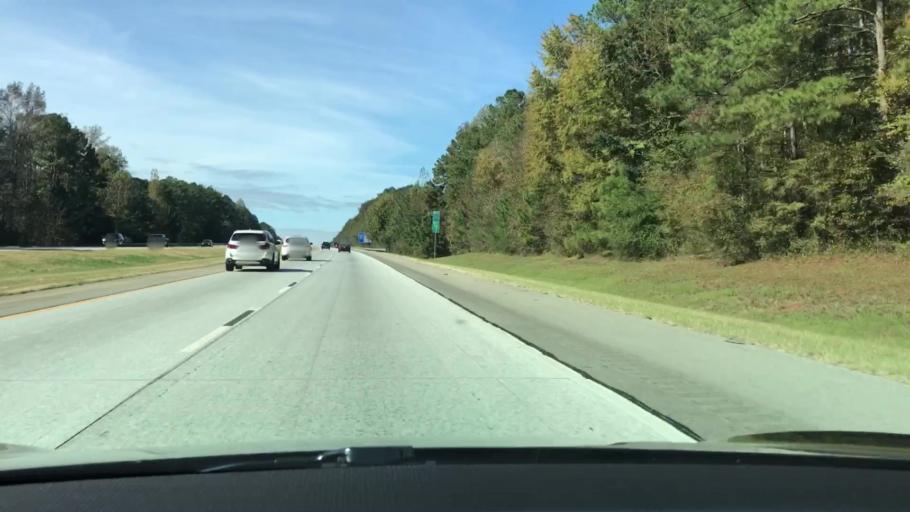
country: US
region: Georgia
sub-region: Morgan County
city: Madison
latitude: 33.5556
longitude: -83.4381
